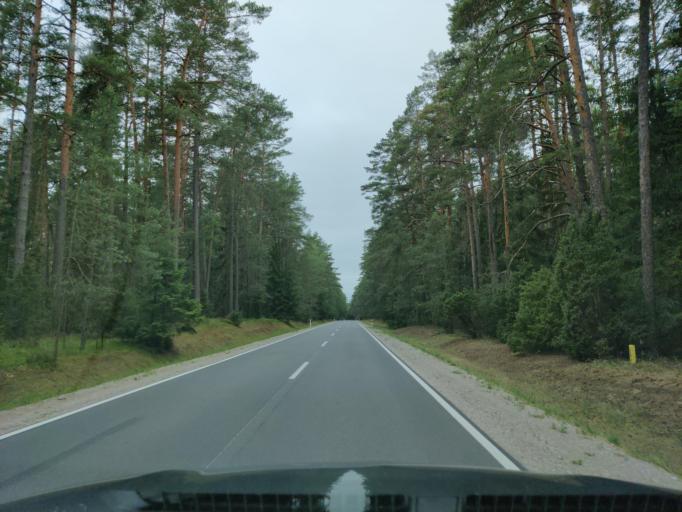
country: PL
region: Masovian Voivodeship
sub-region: Powiat ostrolecki
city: Czarnia
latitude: 53.3349
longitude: 21.2149
